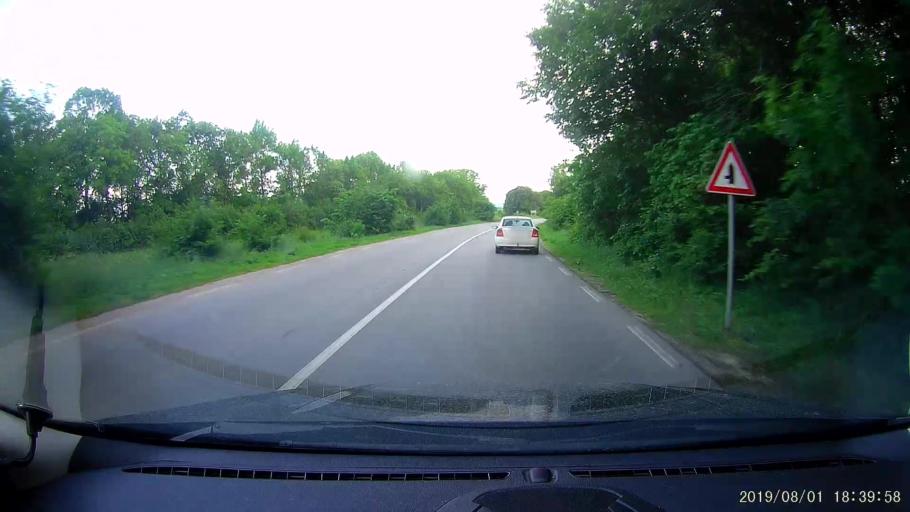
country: BG
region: Shumen
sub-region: Obshtina Khitrino
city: Gara Khitrino
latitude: 43.3753
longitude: 26.9198
